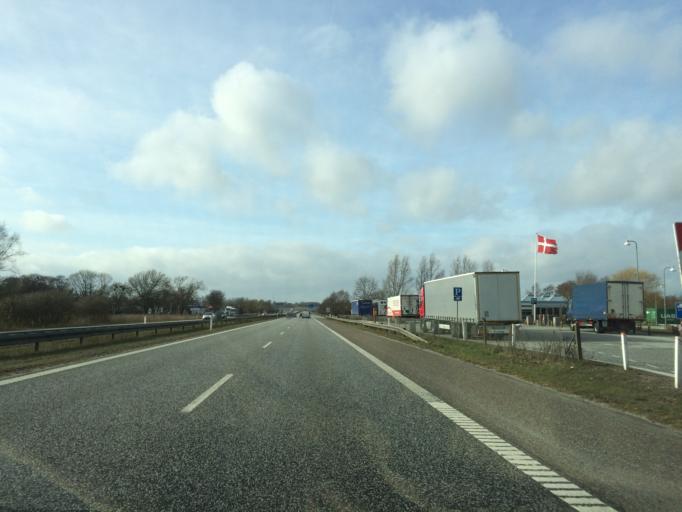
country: DK
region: Central Jutland
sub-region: Randers Kommune
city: Randers
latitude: 56.4482
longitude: 10.0022
